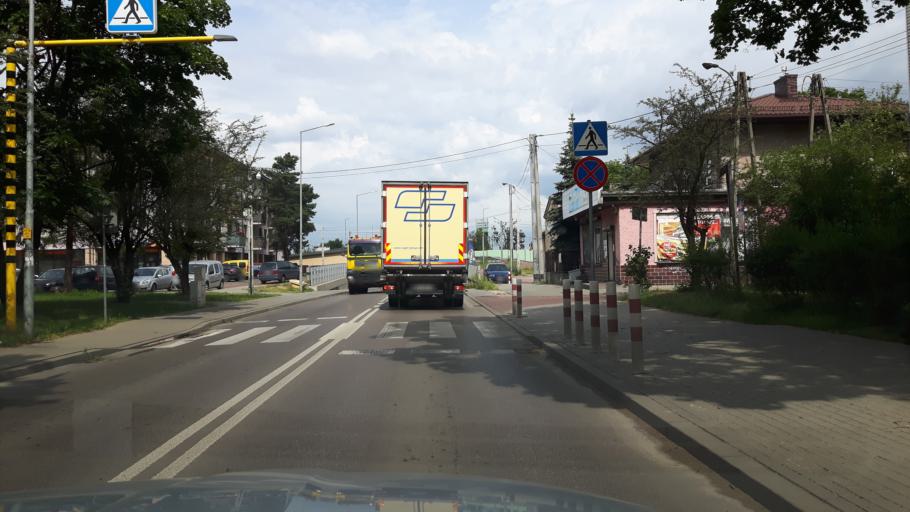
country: PL
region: Masovian Voivodeship
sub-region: Powiat wolominski
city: Nowe Lipiny
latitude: 52.3536
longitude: 21.2590
